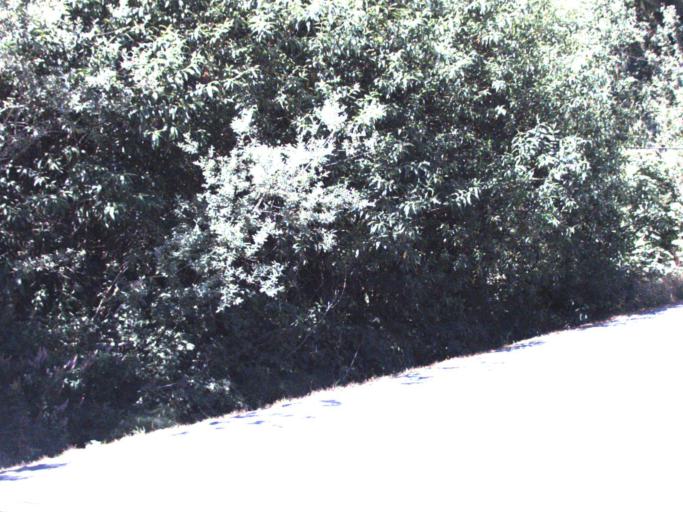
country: US
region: Washington
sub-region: King County
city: East Renton Highlands
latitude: 47.4990
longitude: -122.1169
